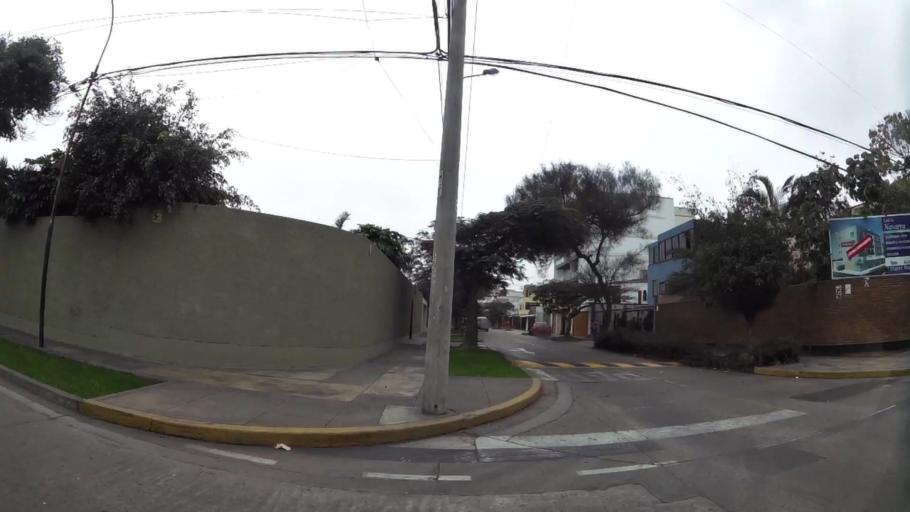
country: PE
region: Lima
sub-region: Lima
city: Surco
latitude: -12.1262
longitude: -76.9927
